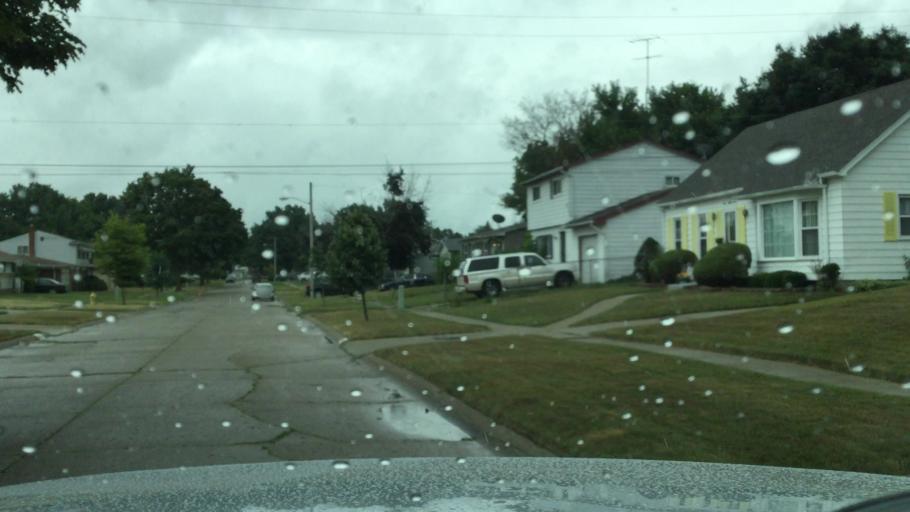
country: US
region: Michigan
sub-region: Genesee County
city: Beecher
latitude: 43.0732
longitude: -83.7226
